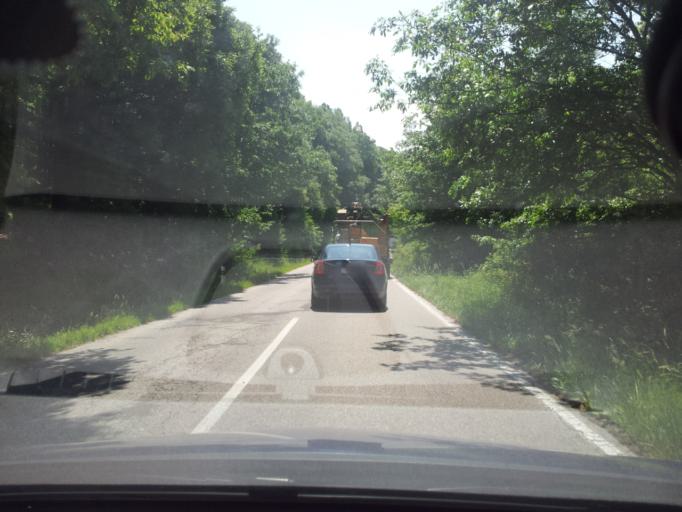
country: SK
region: Nitriansky
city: Partizanske
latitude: 48.5172
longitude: 18.4313
